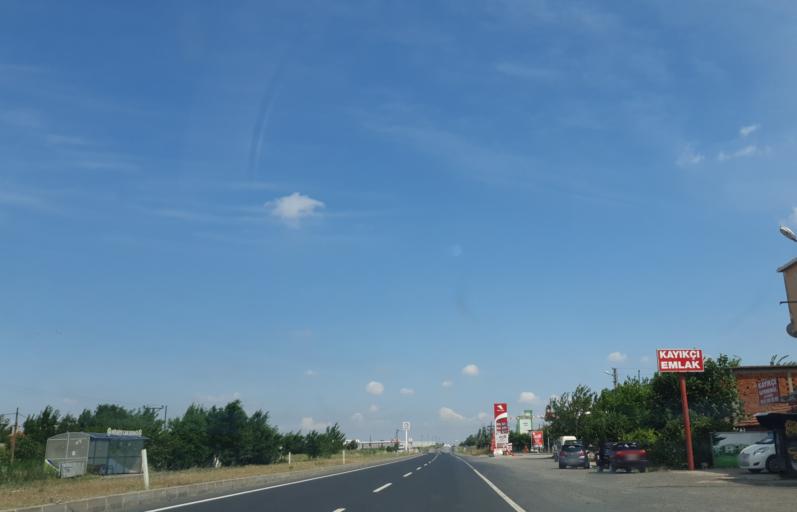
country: TR
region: Tekirdag
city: Beyazkoy
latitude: 41.2640
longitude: 27.6549
